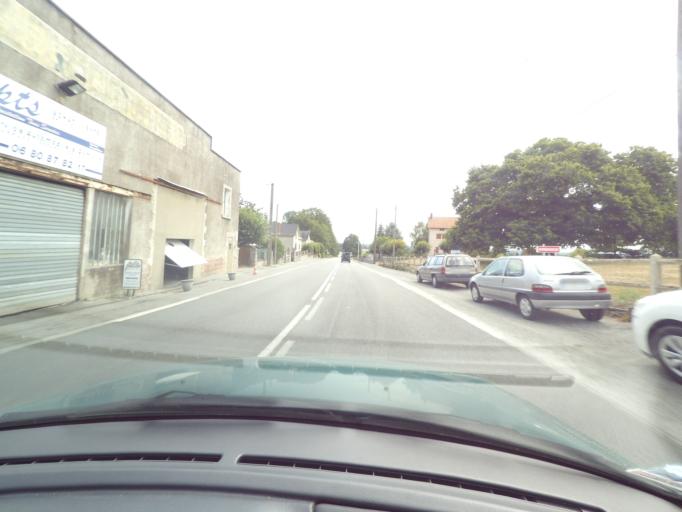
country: FR
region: Limousin
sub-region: Departement de la Haute-Vienne
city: Saint-Paul
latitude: 45.7960
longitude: 1.4252
